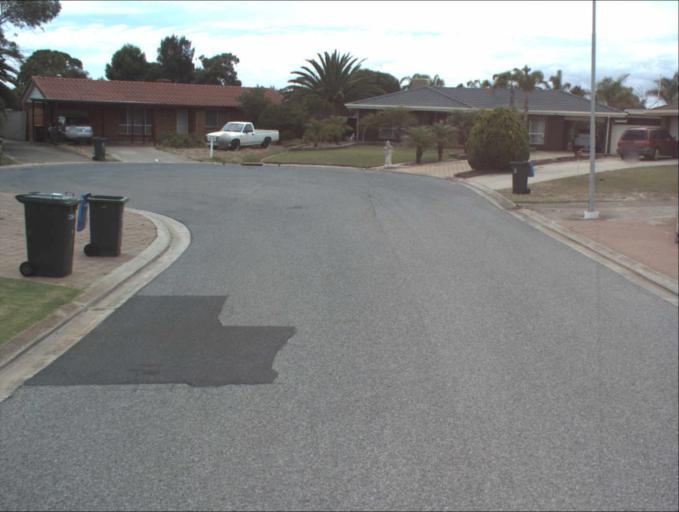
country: AU
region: South Australia
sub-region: Port Adelaide Enfield
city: Birkenhead
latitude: -34.7862
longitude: 138.4926
